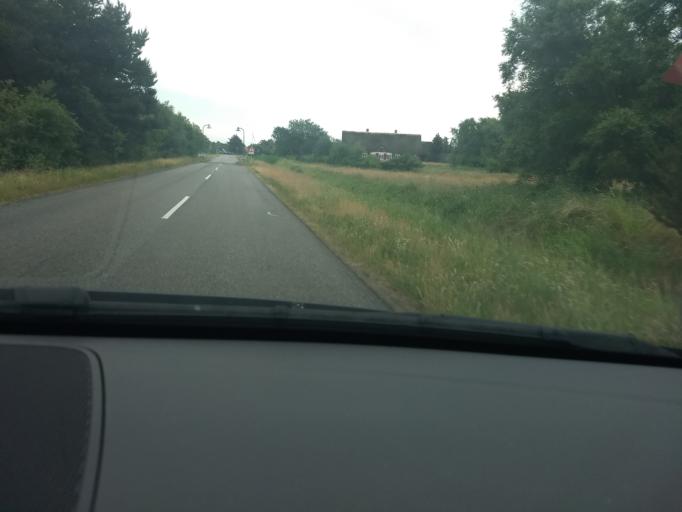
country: DK
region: South Denmark
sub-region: Fano Kommune
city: Nordby
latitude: 55.3553
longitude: 8.4650
